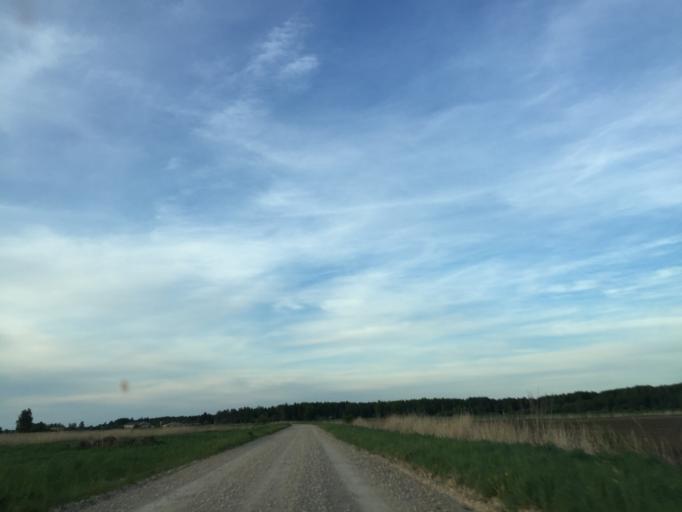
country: LV
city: Tireli
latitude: 56.7791
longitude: 23.5545
